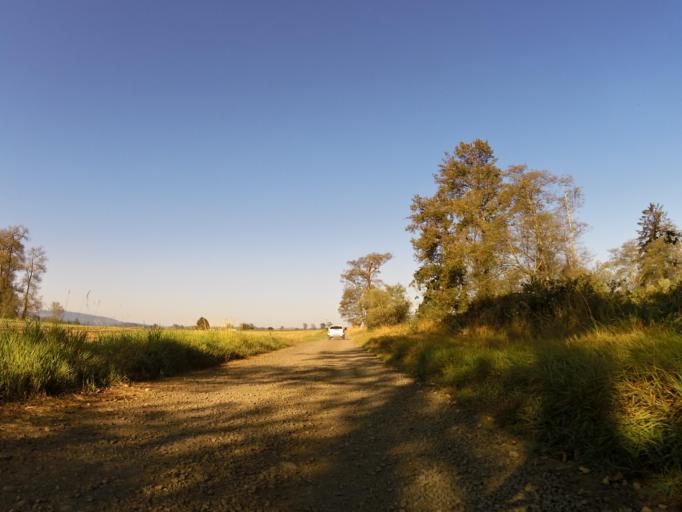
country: US
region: Oregon
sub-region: Tillamook County
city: Tillamook
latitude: 45.4381
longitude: -123.7736
